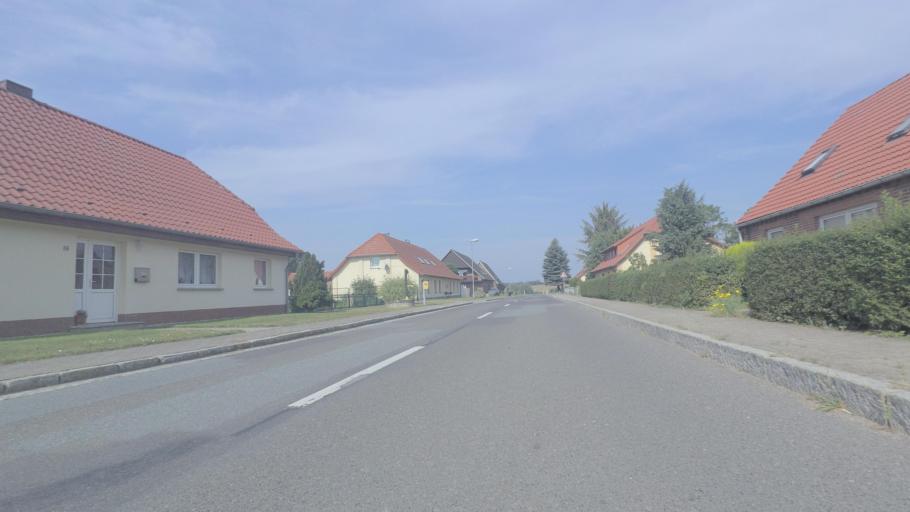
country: DE
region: Mecklenburg-Vorpommern
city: Gielow
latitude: 53.6533
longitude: 12.8011
